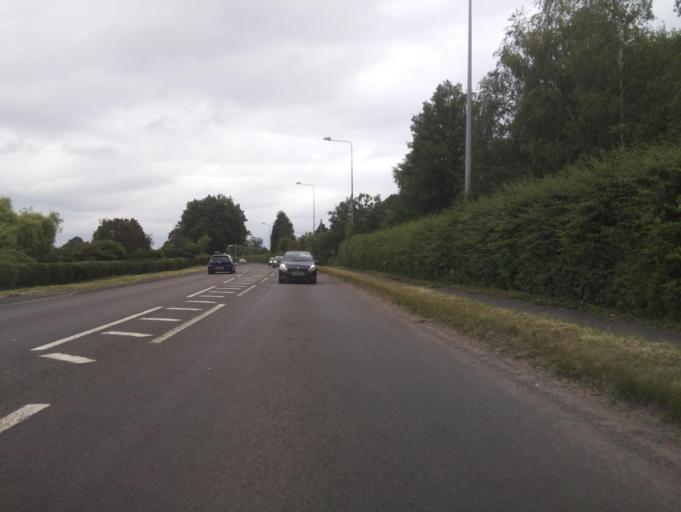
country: GB
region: England
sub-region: Staffordshire
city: Penkridge
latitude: 52.7095
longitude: -2.1236
